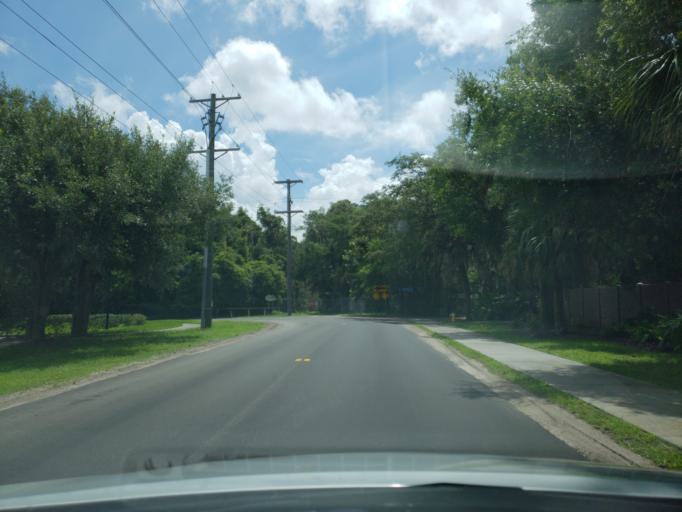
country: US
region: Florida
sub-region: Hillsborough County
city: Riverview
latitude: 27.8864
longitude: -82.3108
